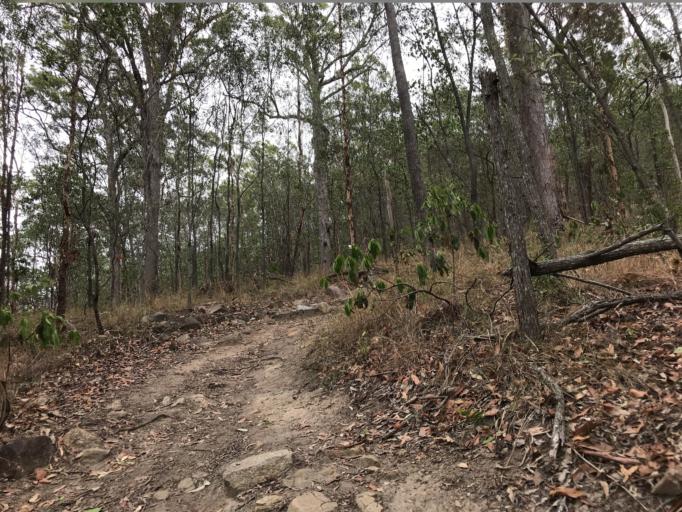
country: AU
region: Queensland
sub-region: Brisbane
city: Taringa
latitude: -27.4647
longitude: 152.9535
